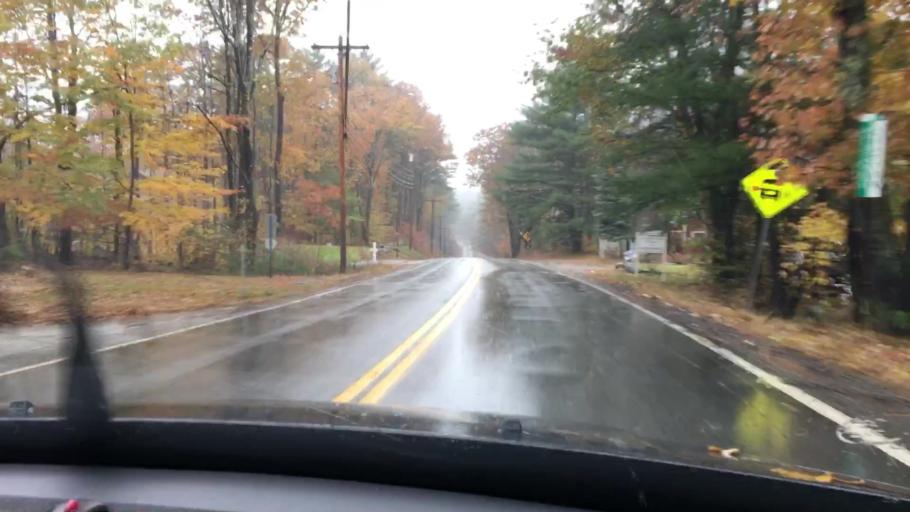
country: US
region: New Hampshire
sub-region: Belknap County
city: Meredith
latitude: 43.7075
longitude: -71.5230
